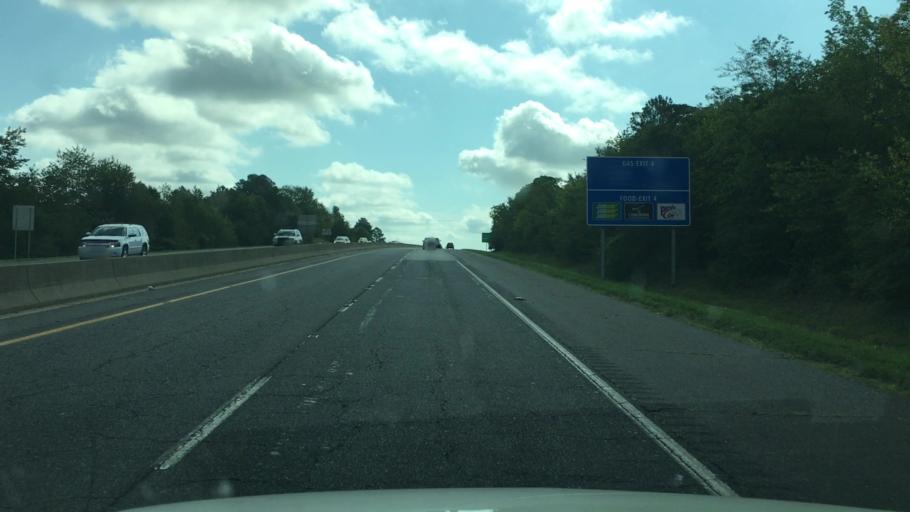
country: US
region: Arkansas
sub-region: Garland County
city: Lake Hamilton
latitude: 34.4658
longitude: -93.0811
